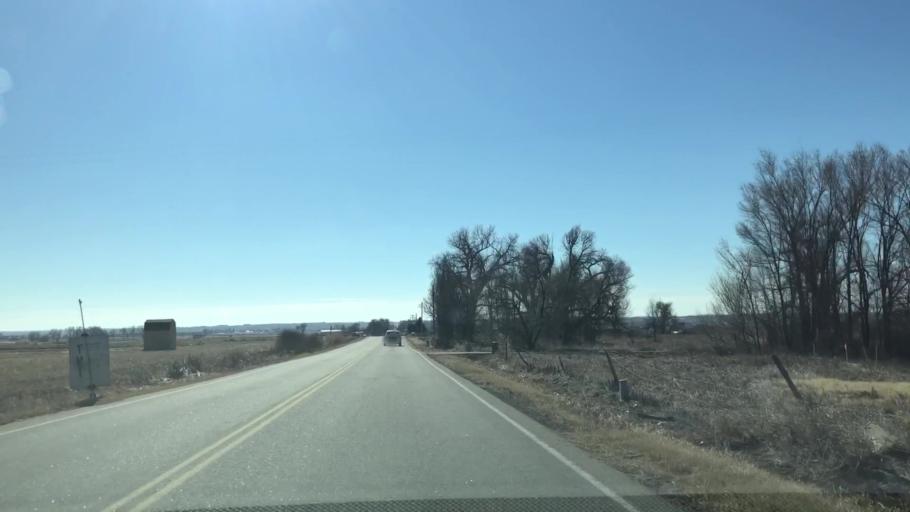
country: US
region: Colorado
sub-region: Weld County
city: Windsor
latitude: 40.5211
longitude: -104.9443
